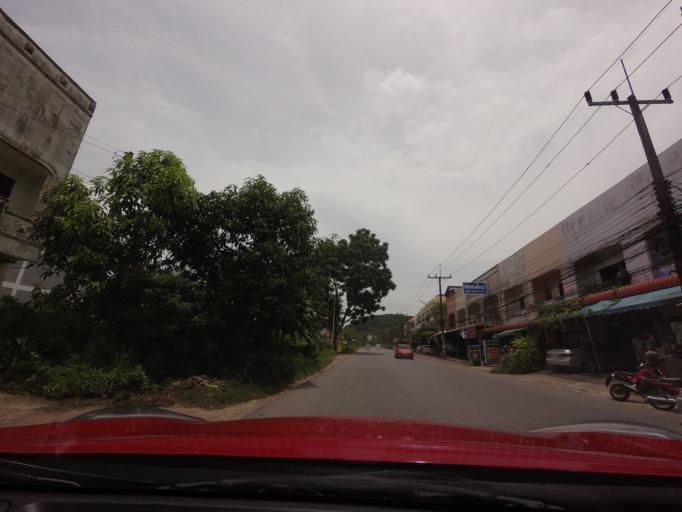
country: TH
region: Songkhla
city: Hat Yai
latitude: 7.0002
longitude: 100.5200
